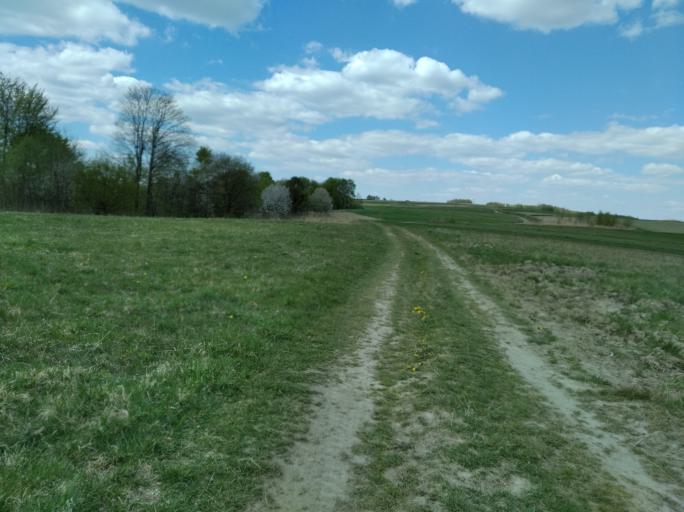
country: PL
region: Subcarpathian Voivodeship
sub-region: Powiat brzozowski
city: Golcowa
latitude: 49.7570
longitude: 22.0709
